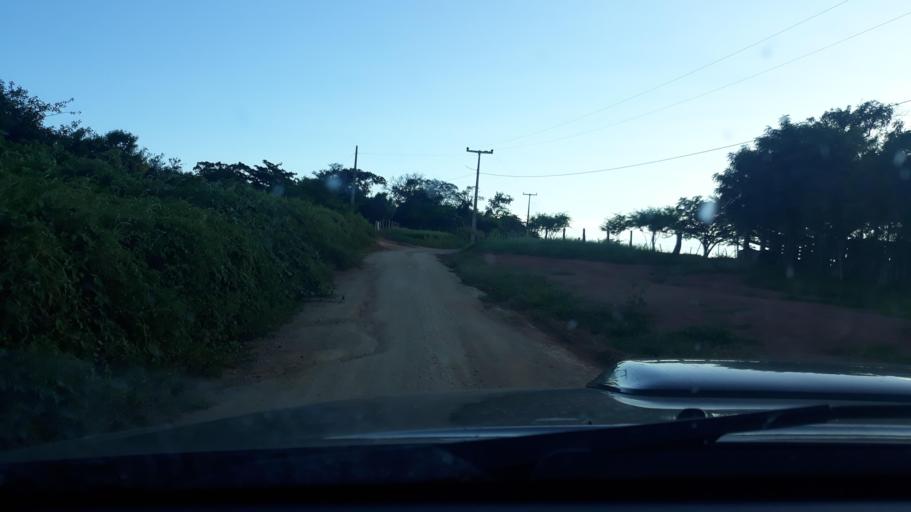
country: BR
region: Bahia
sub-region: Riacho De Santana
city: Riacho de Santana
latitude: -13.8355
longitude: -42.7313
